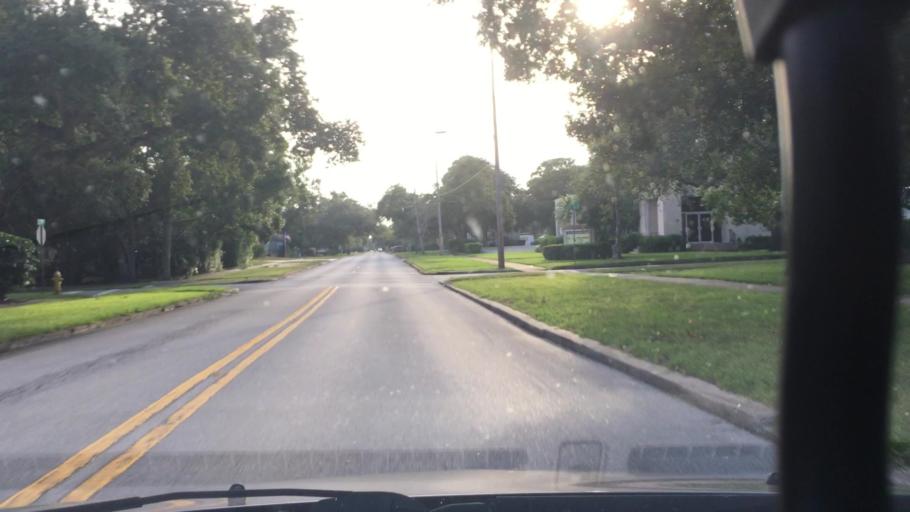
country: US
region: Florida
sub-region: Indian River County
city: Vero Beach
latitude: 27.6421
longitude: -80.4009
